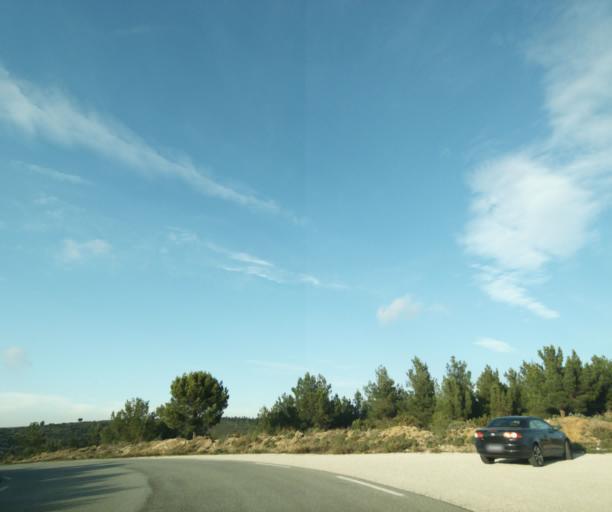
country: FR
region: Provence-Alpes-Cote d'Azur
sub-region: Departement des Bouches-du-Rhone
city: Cassis
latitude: 43.1965
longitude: 5.5567
